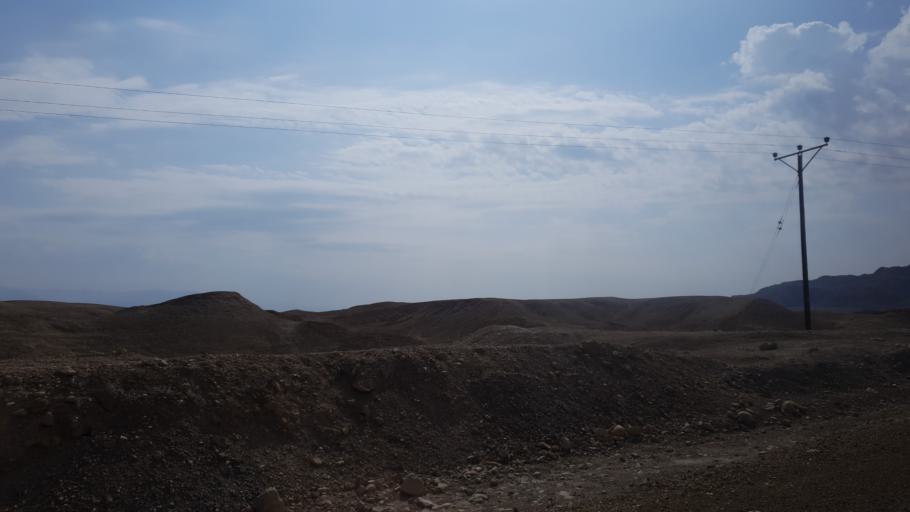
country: IL
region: Southern District
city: `En Boqeq
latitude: 31.3169
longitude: 35.3737
